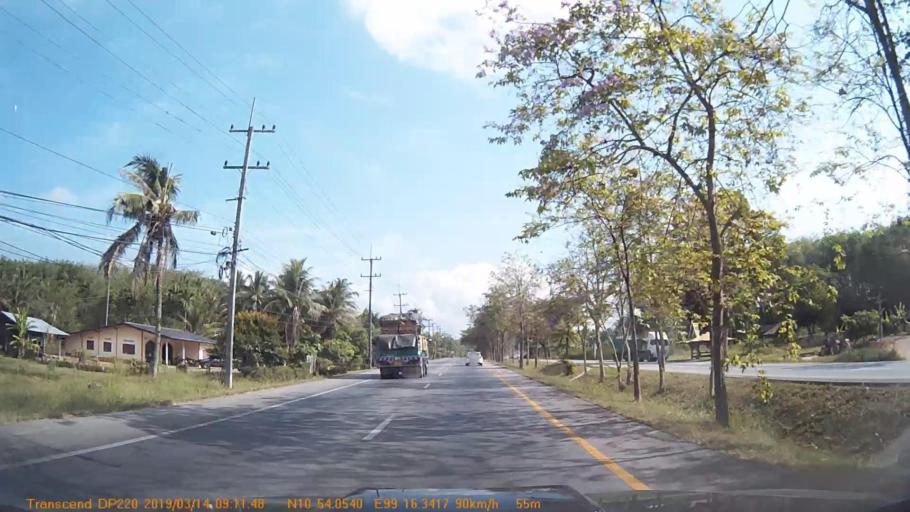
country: TH
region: Chumphon
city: Pathio
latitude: 10.9017
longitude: 99.2725
